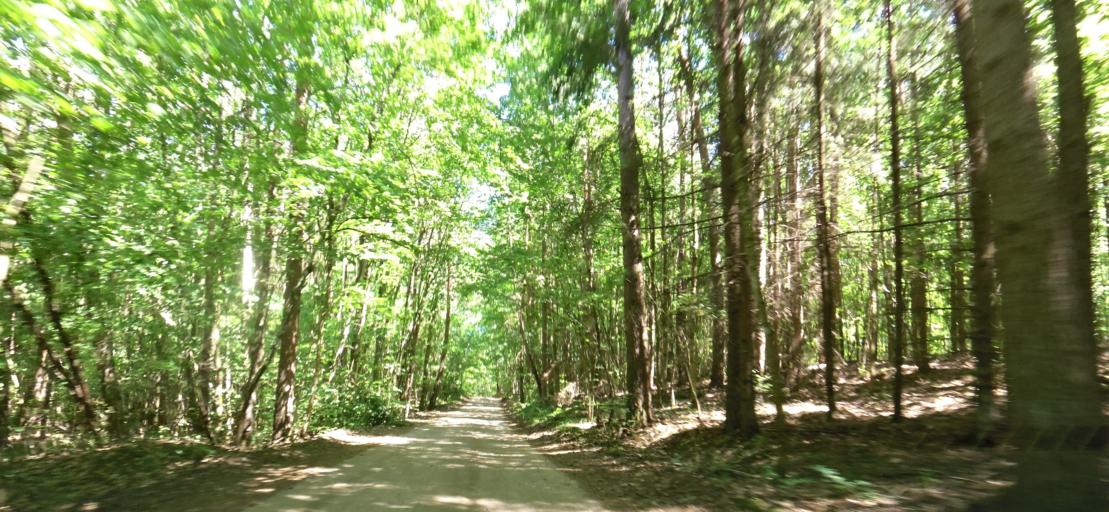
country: LT
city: Grigiskes
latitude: 54.8028
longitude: 24.9945
